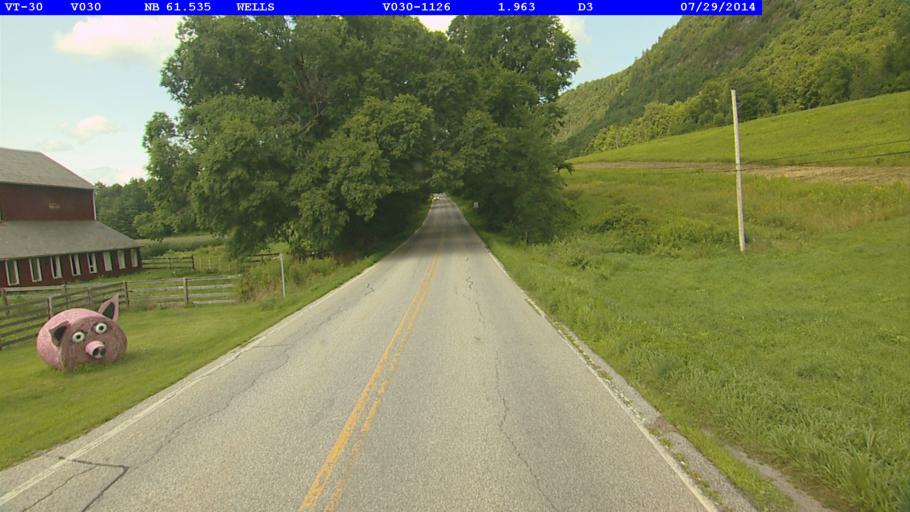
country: US
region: New York
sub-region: Washington County
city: Granville
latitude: 43.4228
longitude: -73.1983
